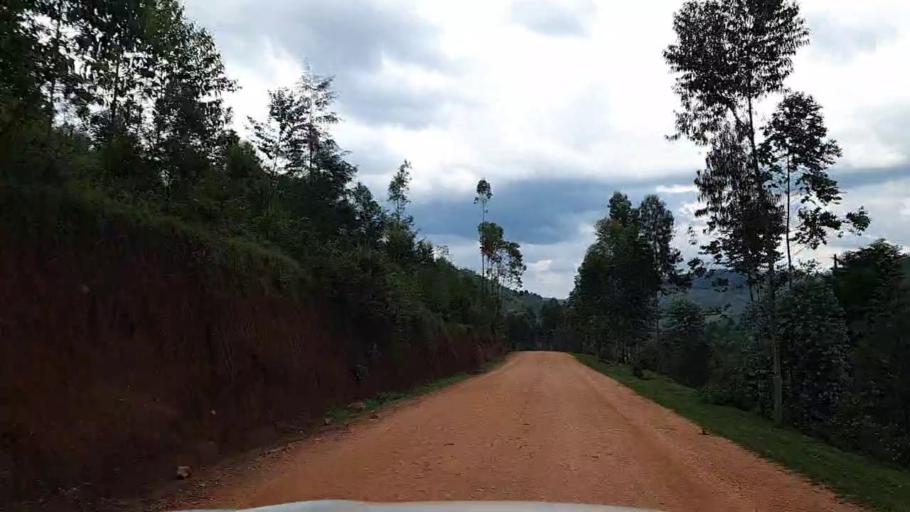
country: RW
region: Southern Province
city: Nyanza
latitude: -2.4035
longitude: 29.6766
